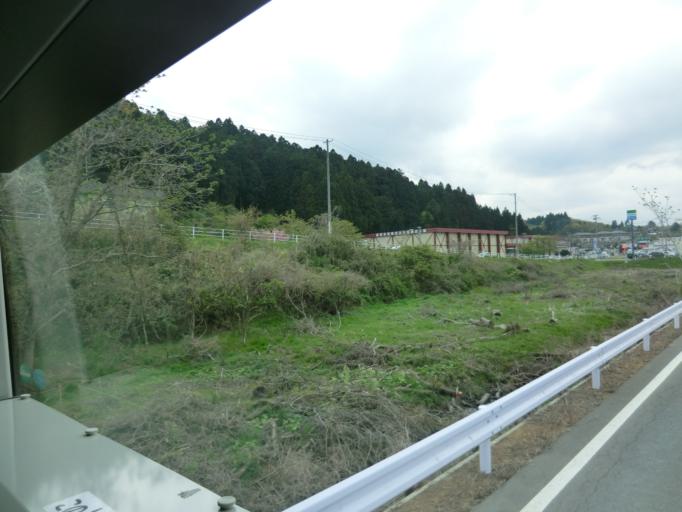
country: JP
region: Iwate
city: Ofunato
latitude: 38.9007
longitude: 141.5563
